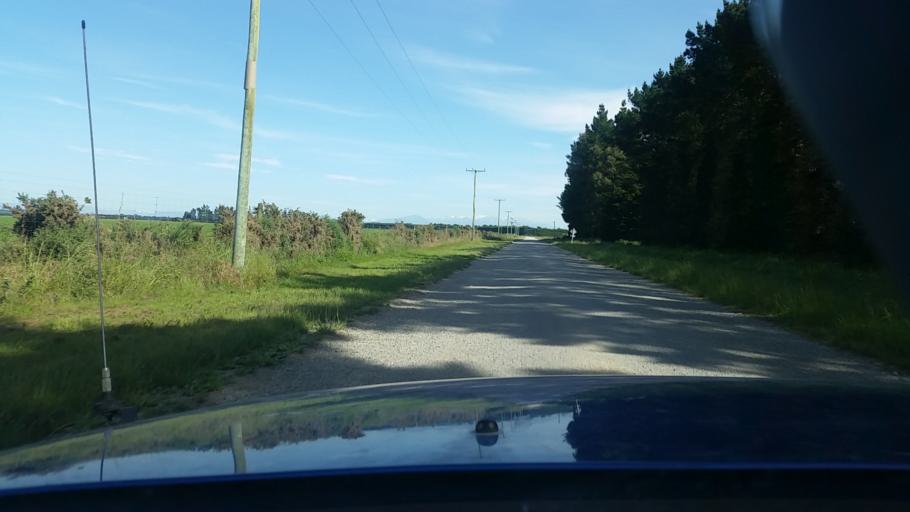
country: NZ
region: Canterbury
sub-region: Ashburton District
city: Ashburton
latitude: -43.9626
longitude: 171.8915
